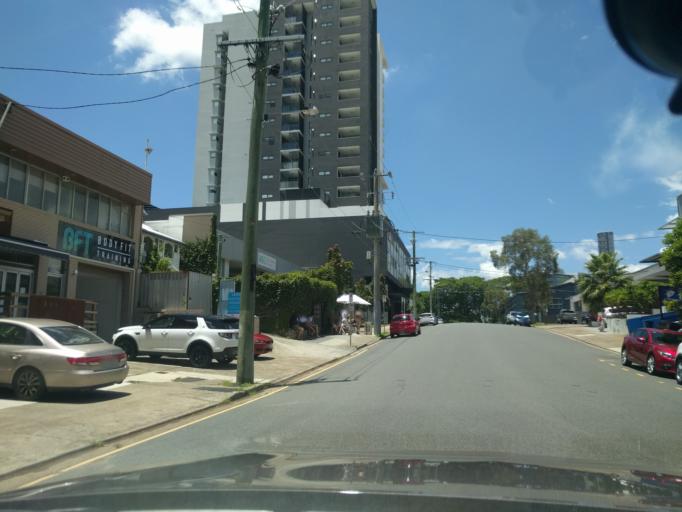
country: AU
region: Queensland
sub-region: Brisbane
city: Milton
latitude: -27.4692
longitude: 153.0061
